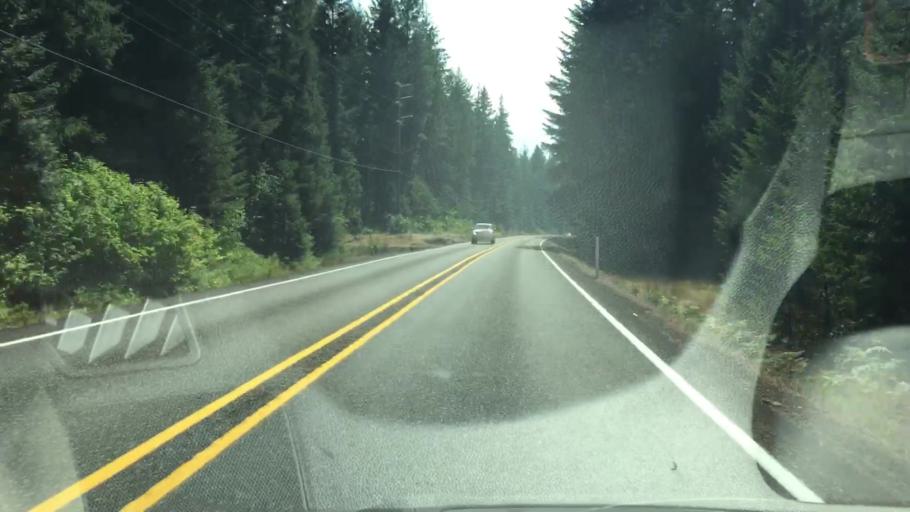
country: US
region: Washington
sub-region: Klickitat County
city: White Salmon
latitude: 45.9151
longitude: -121.4997
